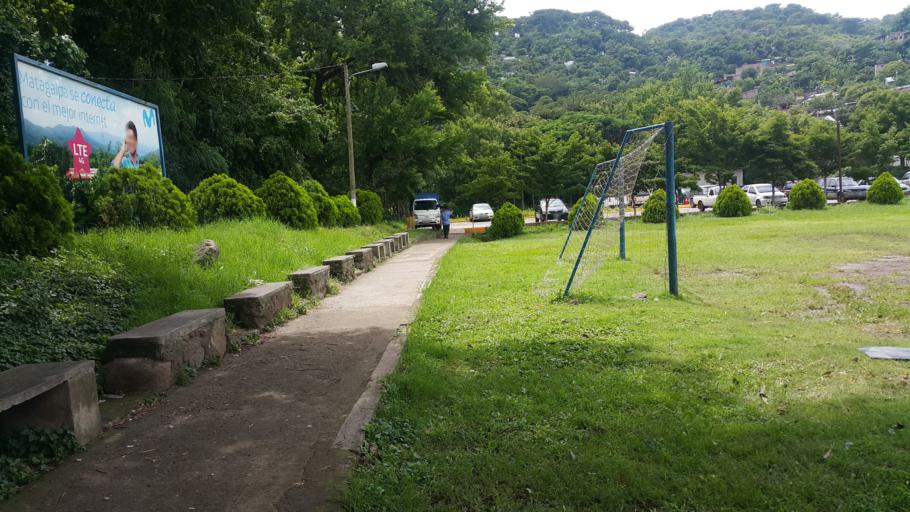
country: NI
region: Matagalpa
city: Matagalpa
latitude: 12.9234
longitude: -85.9228
